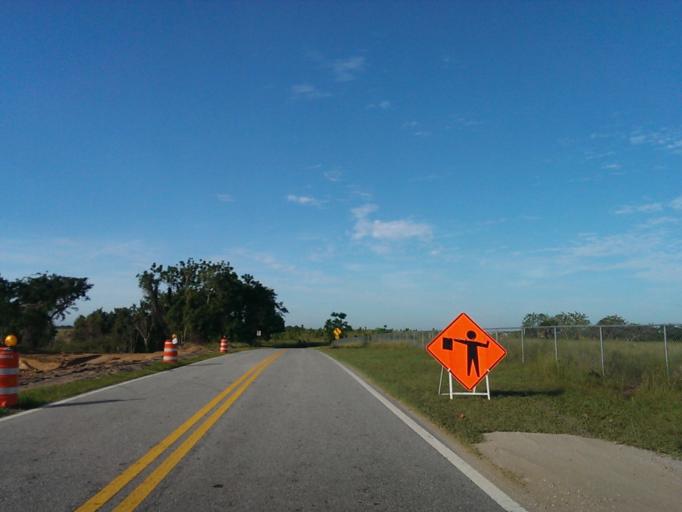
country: US
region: Florida
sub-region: Polk County
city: Citrus Ridge
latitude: 28.4283
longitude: -81.6175
